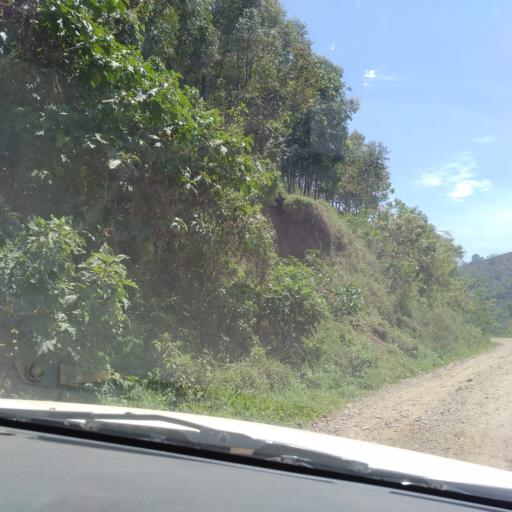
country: CD
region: Nord Kivu
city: Sake
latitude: -1.9732
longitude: 28.9140
